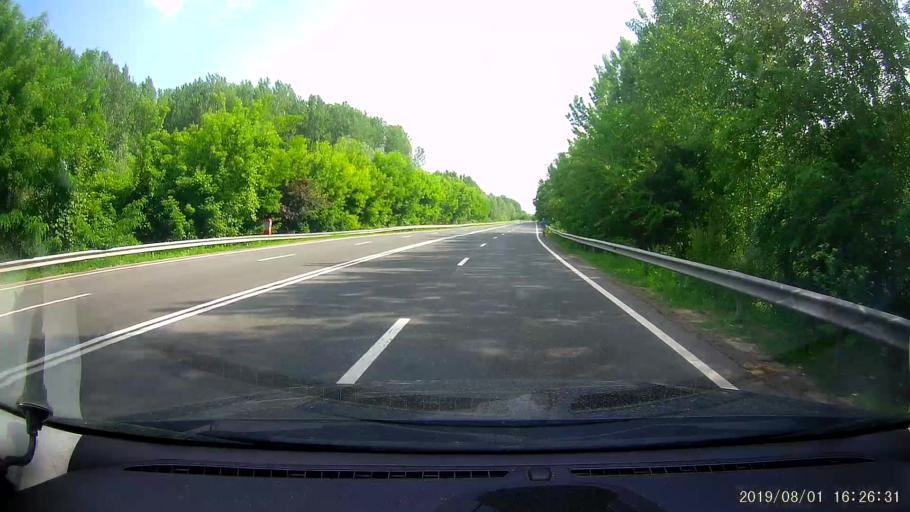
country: RO
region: Calarasi
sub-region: Municipiul Calarasi
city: Calarasi
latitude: 44.1783
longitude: 27.3214
